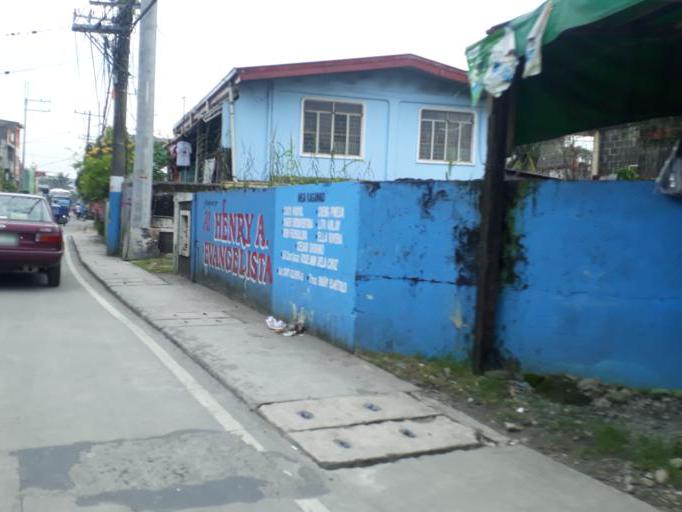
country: PH
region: Calabarzon
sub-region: Province of Rizal
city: Valenzuela
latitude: 14.7004
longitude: 120.9571
